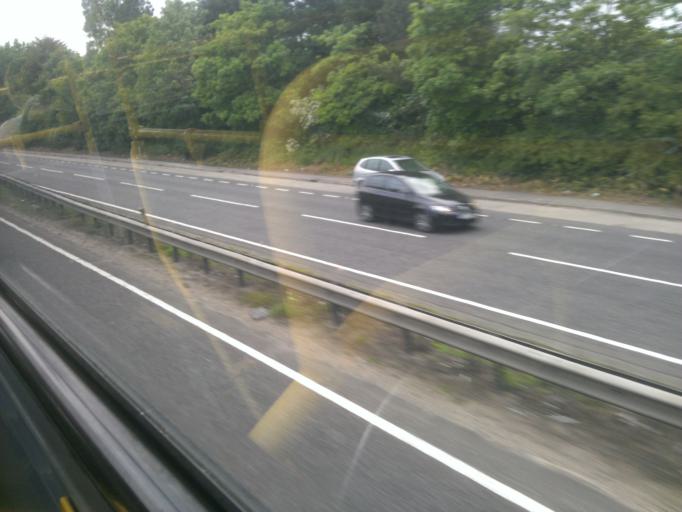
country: GB
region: England
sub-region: Suffolk
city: East Bergholt
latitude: 51.9482
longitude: 0.9590
